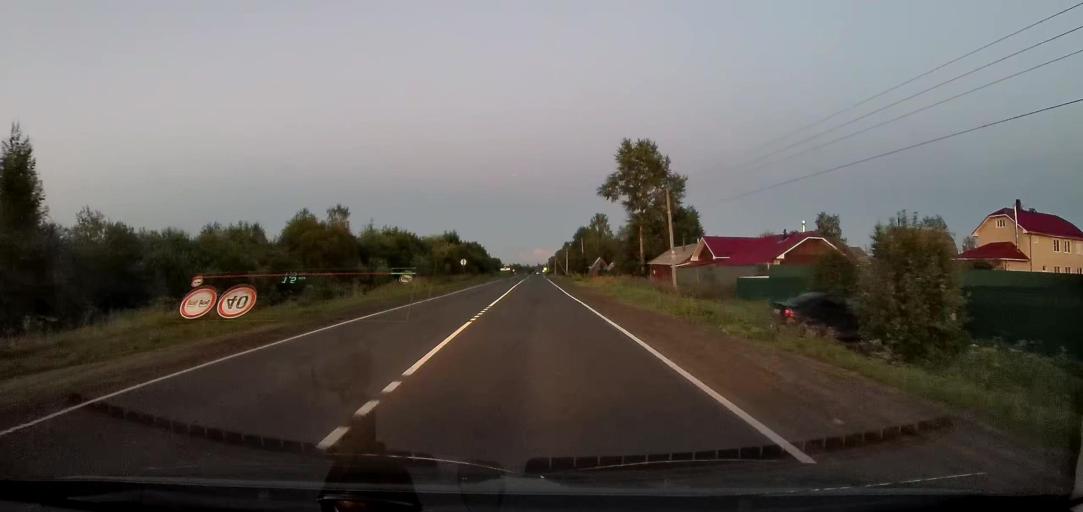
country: RU
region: Arkhangelskaya
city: Uyemskiy
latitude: 64.4460
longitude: 40.9485
